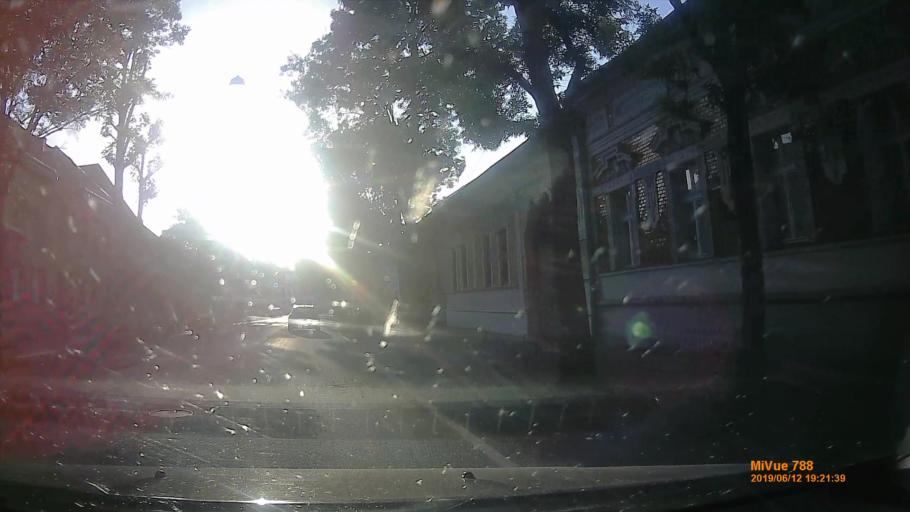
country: HU
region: Bacs-Kiskun
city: Kecskemet
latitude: 46.9056
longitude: 19.6987
